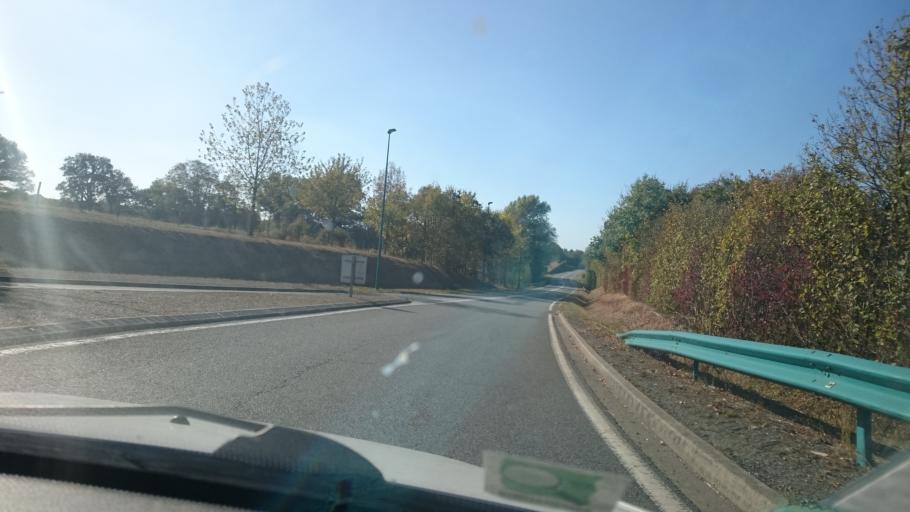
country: FR
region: Centre
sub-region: Departement du Cher
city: Chateaumeillant
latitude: 46.5551
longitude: 2.1994
